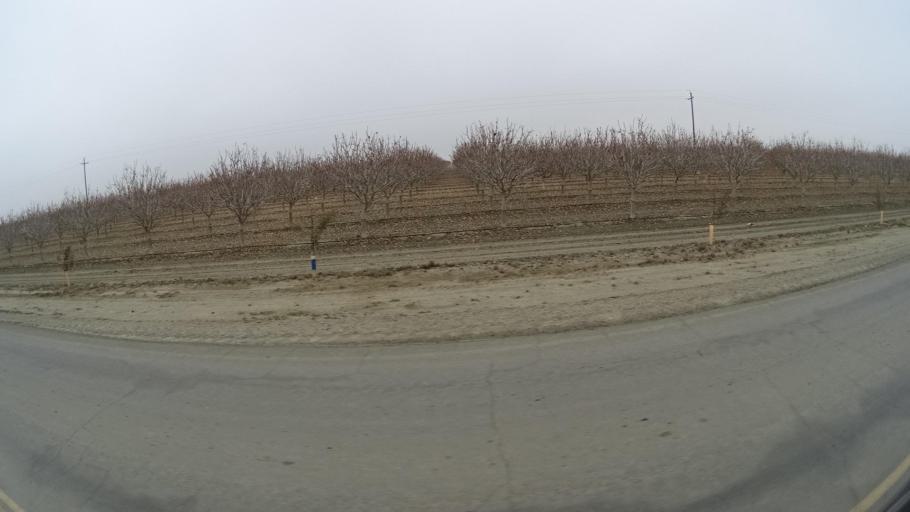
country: US
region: California
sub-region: Kern County
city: Rosedale
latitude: 35.2093
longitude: -119.2310
